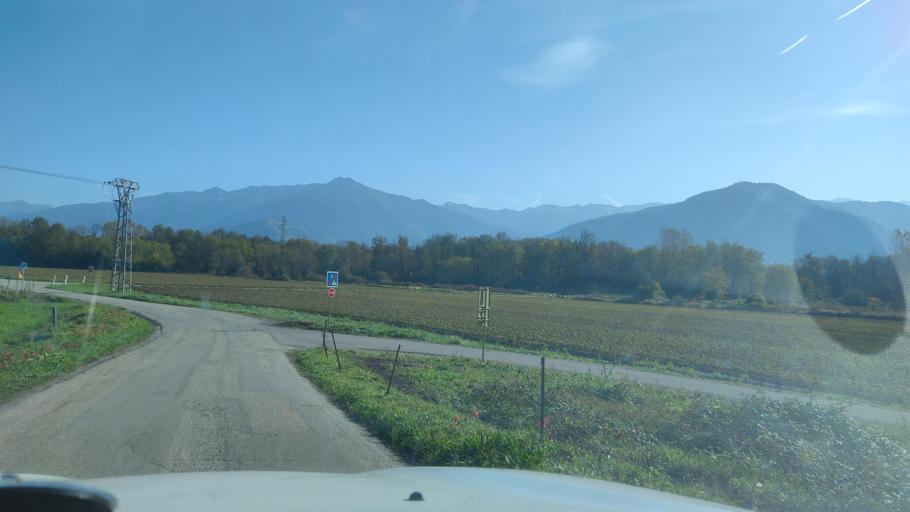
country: FR
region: Rhone-Alpes
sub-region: Departement de la Savoie
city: Coise-Saint-Jean-Pied-Gauthier
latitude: 45.5610
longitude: 6.1739
